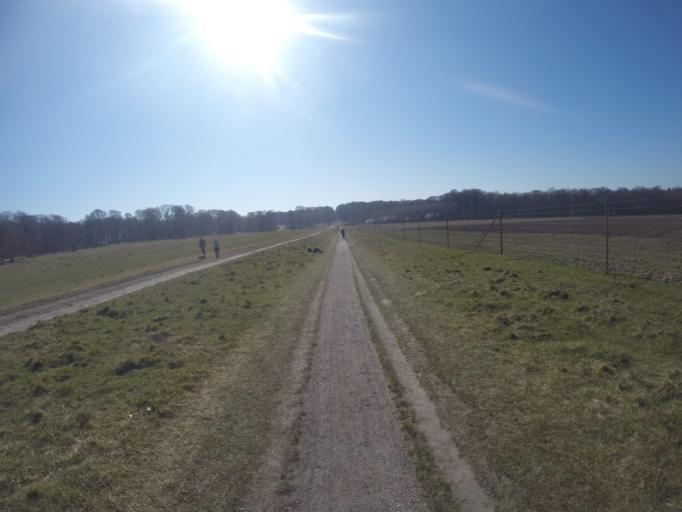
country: DK
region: Capital Region
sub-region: Gentofte Kommune
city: Charlottenlund
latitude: 55.7887
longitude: 12.5624
